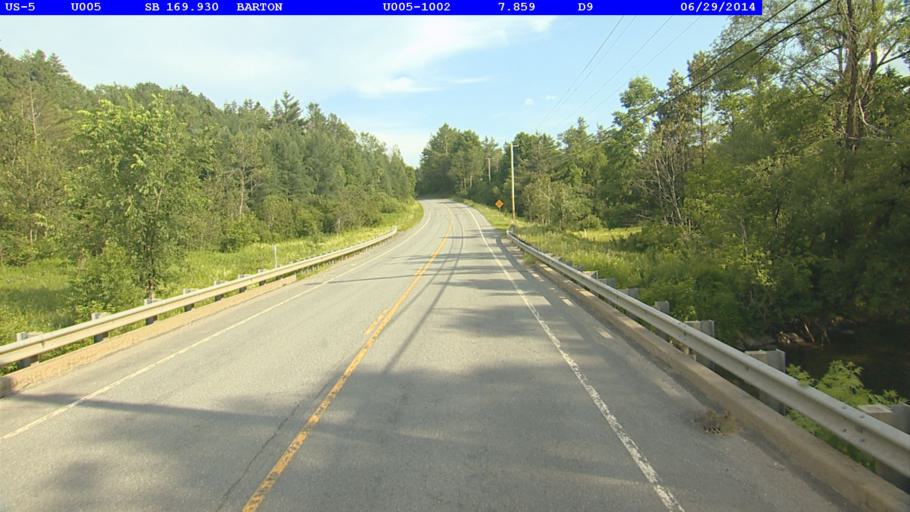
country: US
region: Vermont
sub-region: Orleans County
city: Newport
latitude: 44.7714
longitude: -72.2086
